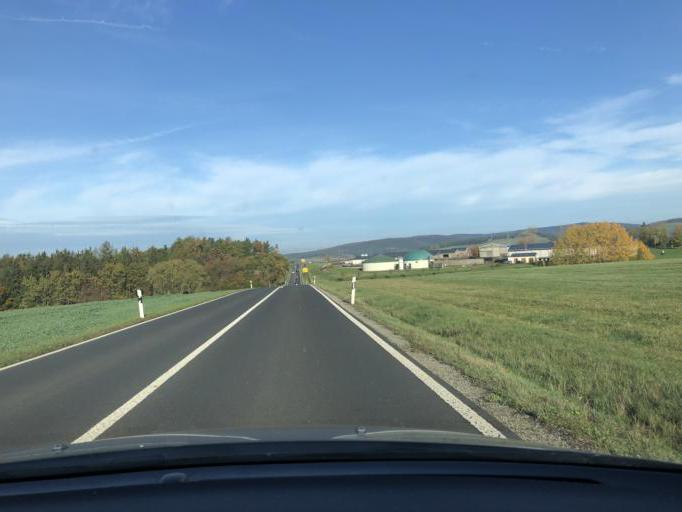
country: DE
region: Thuringia
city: Ehrenberg
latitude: 50.4750
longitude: 10.6543
